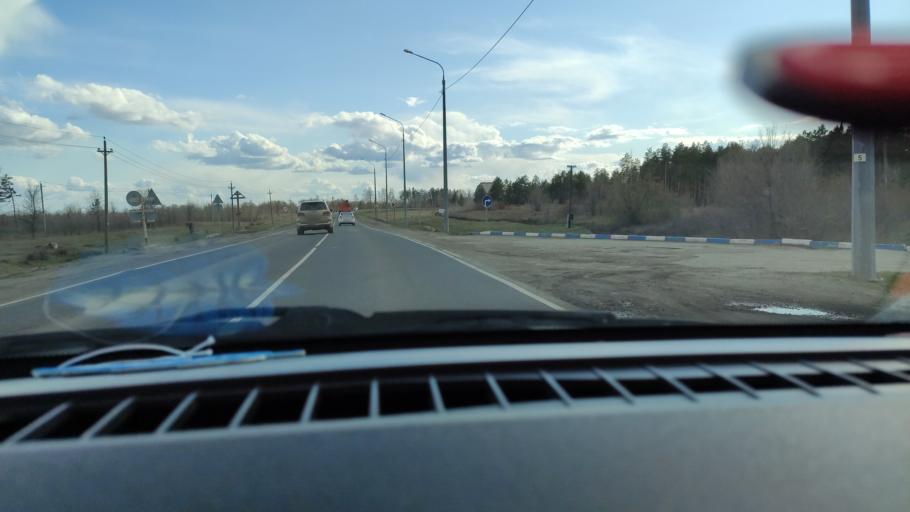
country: RU
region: Saratov
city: Sennoy
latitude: 52.1470
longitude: 46.9457
